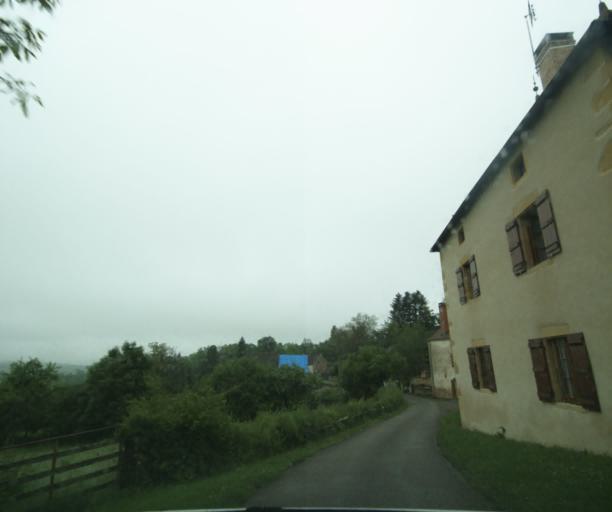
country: FR
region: Bourgogne
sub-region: Departement de Saone-et-Loire
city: Charolles
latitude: 46.4002
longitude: 4.1952
